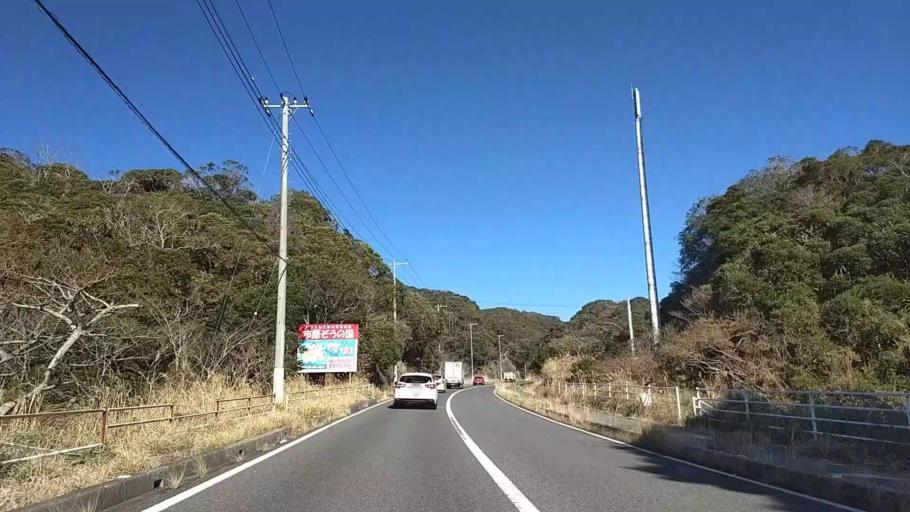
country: JP
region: Chiba
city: Katsuura
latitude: 35.1224
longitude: 140.2295
